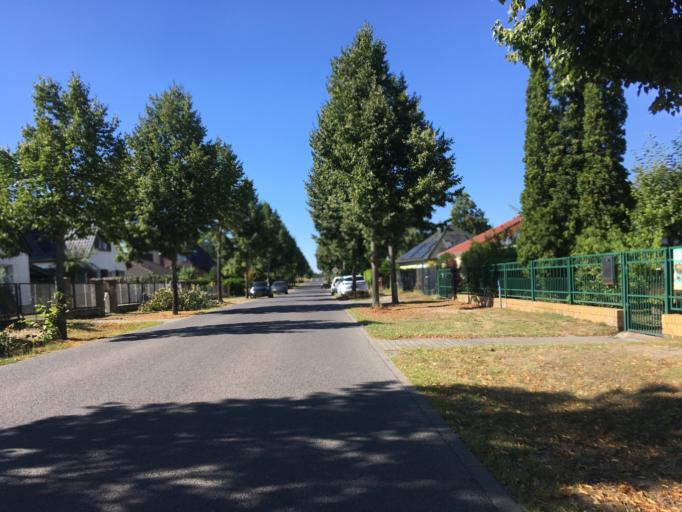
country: DE
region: Brandenburg
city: Schulzendorf
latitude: 52.3585
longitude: 13.5864
